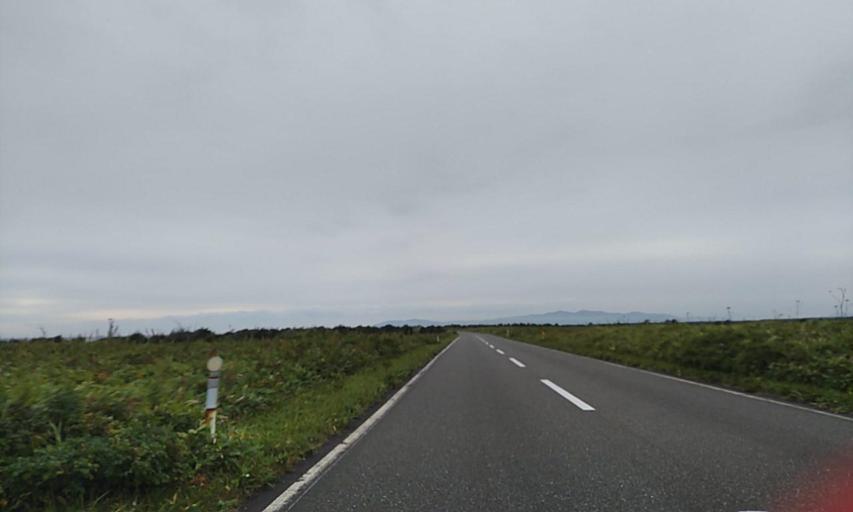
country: JP
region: Hokkaido
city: Makubetsu
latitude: 45.2593
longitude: 142.2472
